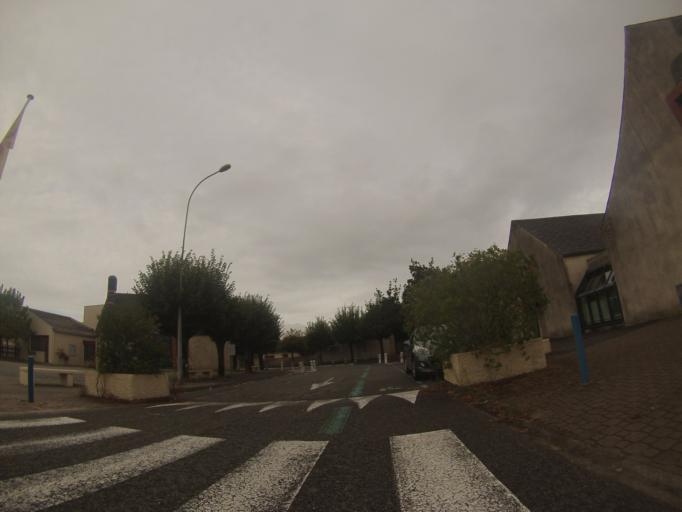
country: FR
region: Aquitaine
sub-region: Departement des Pyrenees-Atlantiques
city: Bizanos
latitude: 43.2776
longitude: -0.3560
